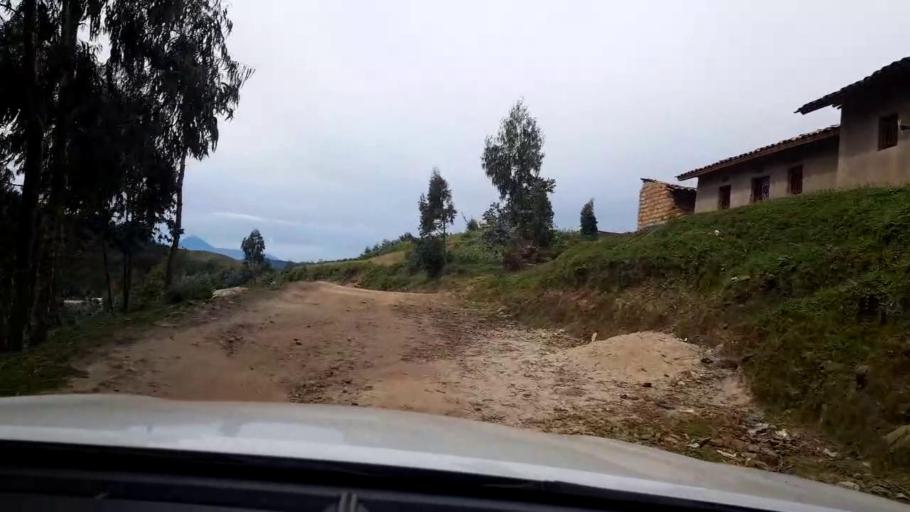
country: RW
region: Western Province
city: Kibuye
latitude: -1.8794
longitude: 29.4554
